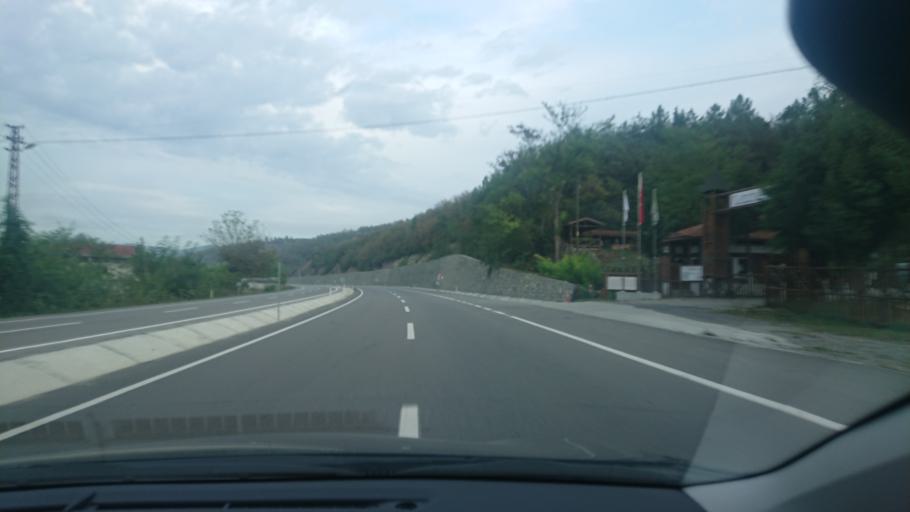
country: TR
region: Zonguldak
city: Beycuma
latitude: 41.3318
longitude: 32.0443
